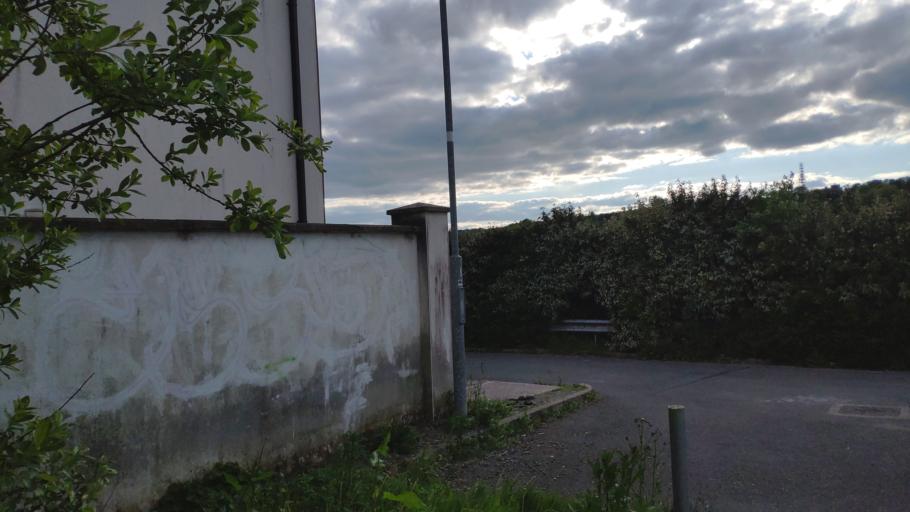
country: IE
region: Munster
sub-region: County Cork
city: Cork
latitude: 51.9098
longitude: -8.4707
